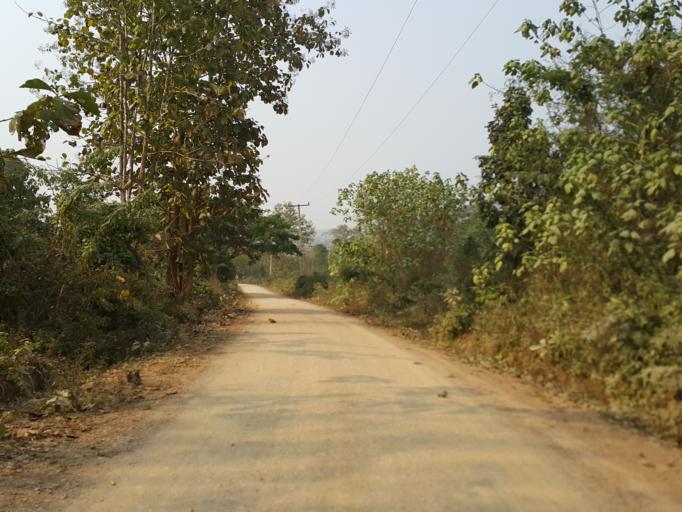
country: TH
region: Lamphun
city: Li
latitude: 17.6033
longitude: 98.9712
